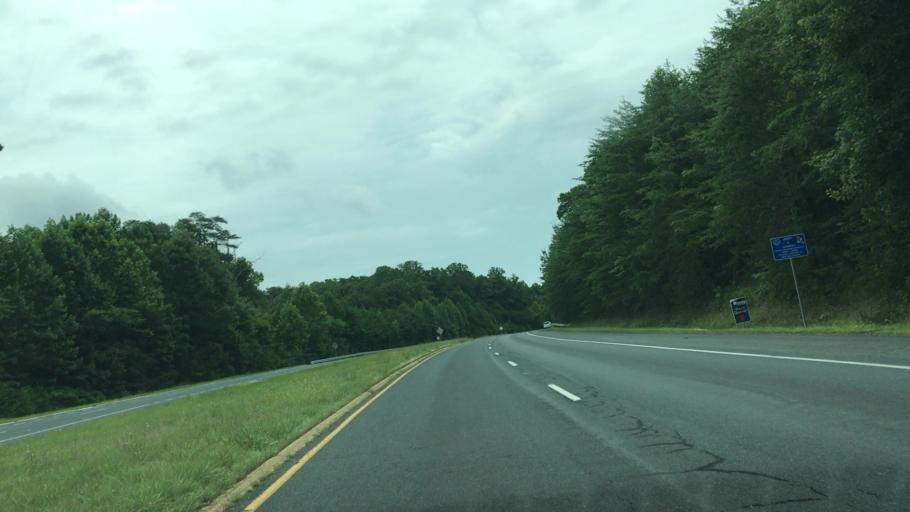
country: US
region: Virginia
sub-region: Prince William County
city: Buckhall
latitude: 38.6978
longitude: -77.4005
